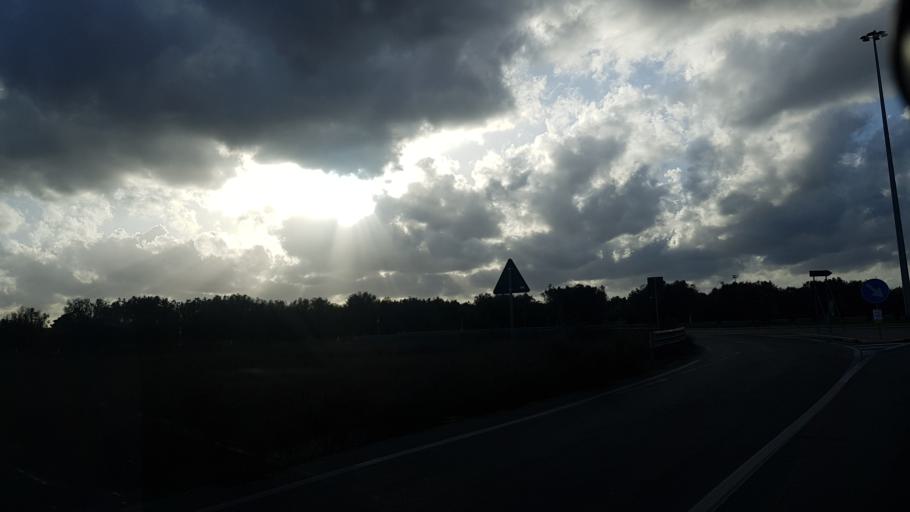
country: IT
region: Apulia
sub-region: Provincia di Brindisi
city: San Pietro Vernotico
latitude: 40.4876
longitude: 18.0116
